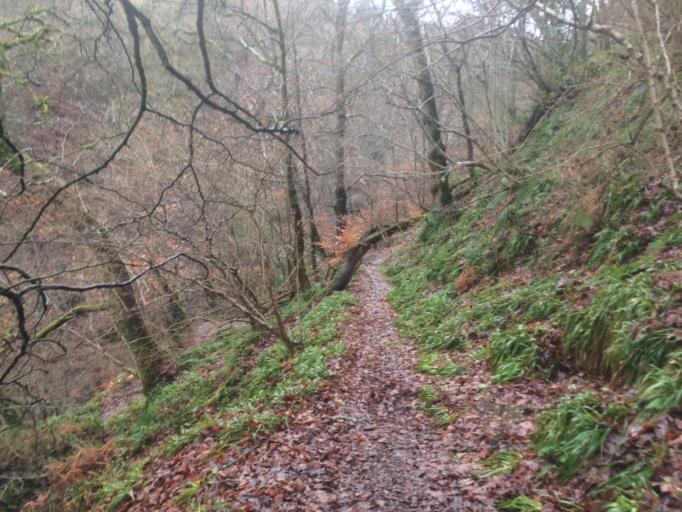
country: GB
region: Scotland
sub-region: Midlothian
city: Loanhead
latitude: 55.8567
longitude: -3.1523
